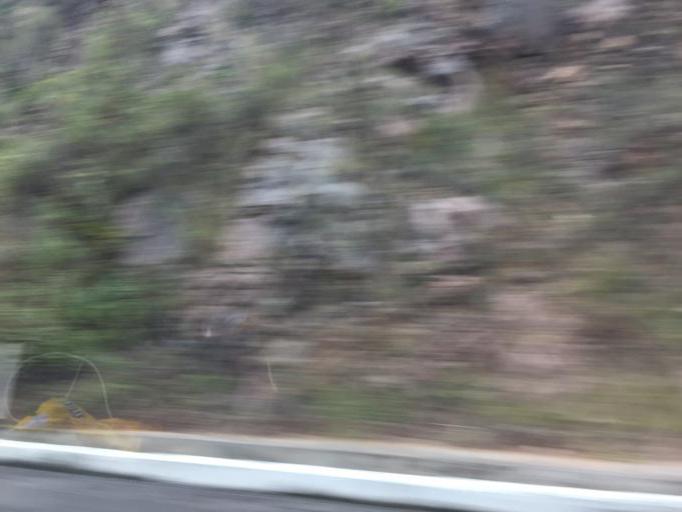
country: MX
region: Michoacan
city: Panindicuaro de la Reforma
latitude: 19.9737
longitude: -101.7354
